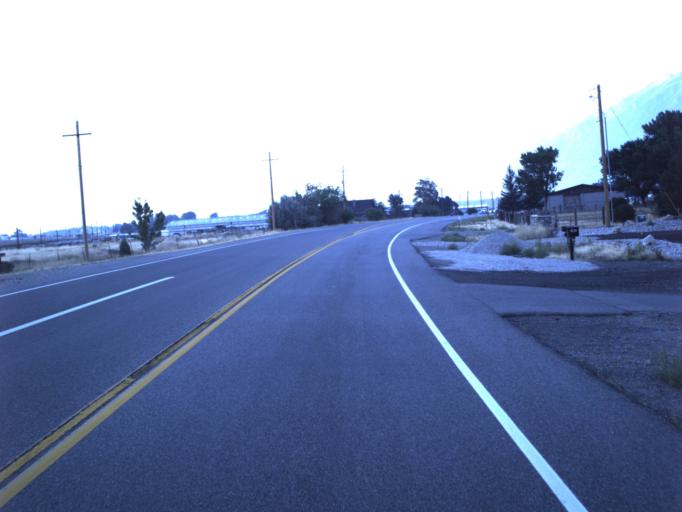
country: US
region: Utah
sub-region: Utah County
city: Mapleton
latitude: 40.1030
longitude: -111.5973
